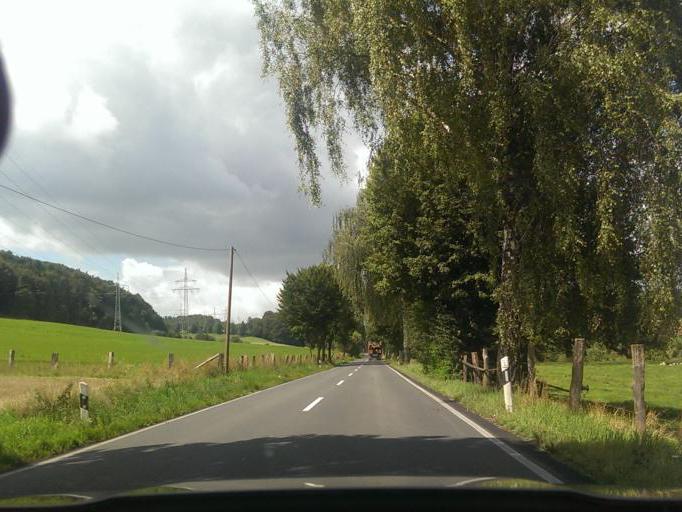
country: DE
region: North Rhine-Westphalia
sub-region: Regierungsbezirk Detmold
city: Hoexter
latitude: 51.8205
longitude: 9.3879
